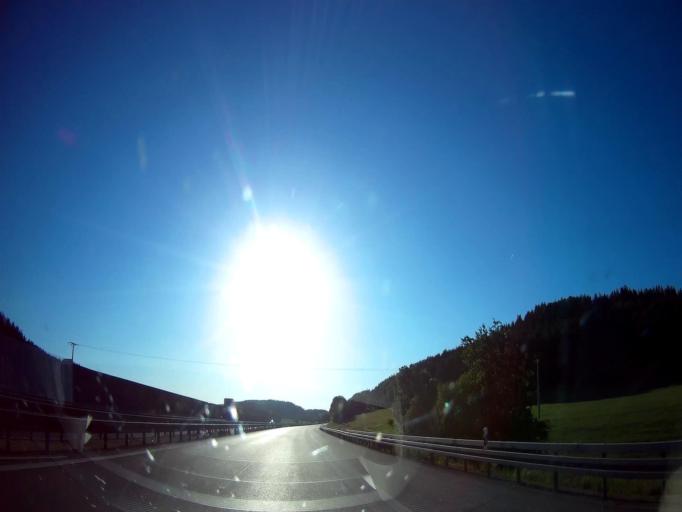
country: DE
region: Bavaria
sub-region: Upper Palatinate
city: Deining
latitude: 49.2832
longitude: 11.5741
